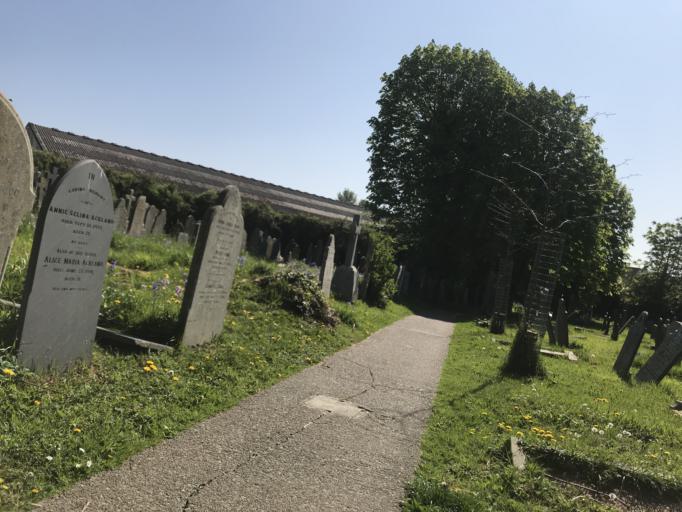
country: GB
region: England
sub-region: Devon
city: Barnstaple
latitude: 51.0758
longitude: -4.0533
